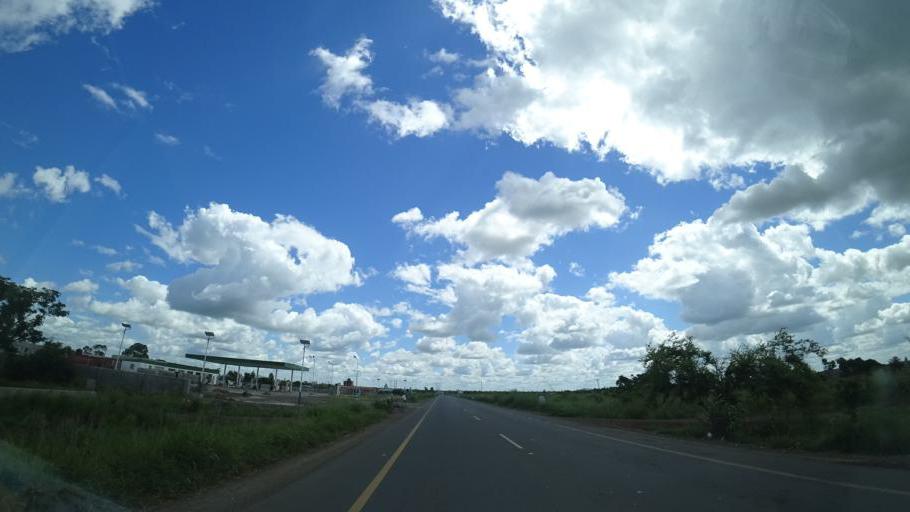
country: MZ
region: Sofala
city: Dondo
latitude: -19.2833
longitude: 34.2232
